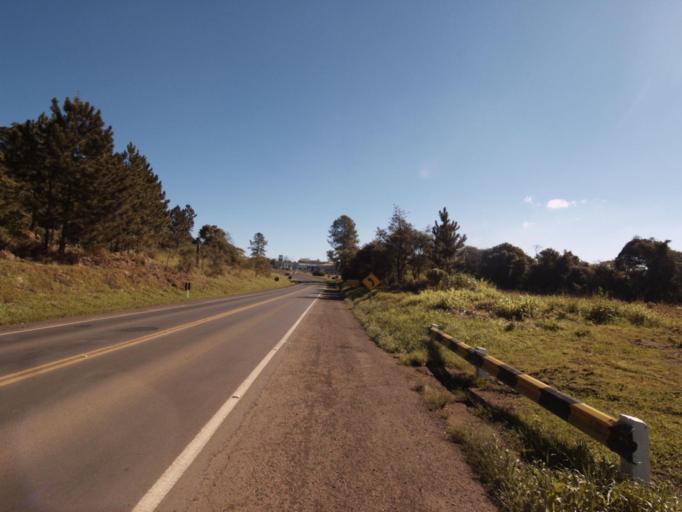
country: BR
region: Santa Catarina
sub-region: Joacaba
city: Joacaba
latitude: -27.1782
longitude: -51.5240
